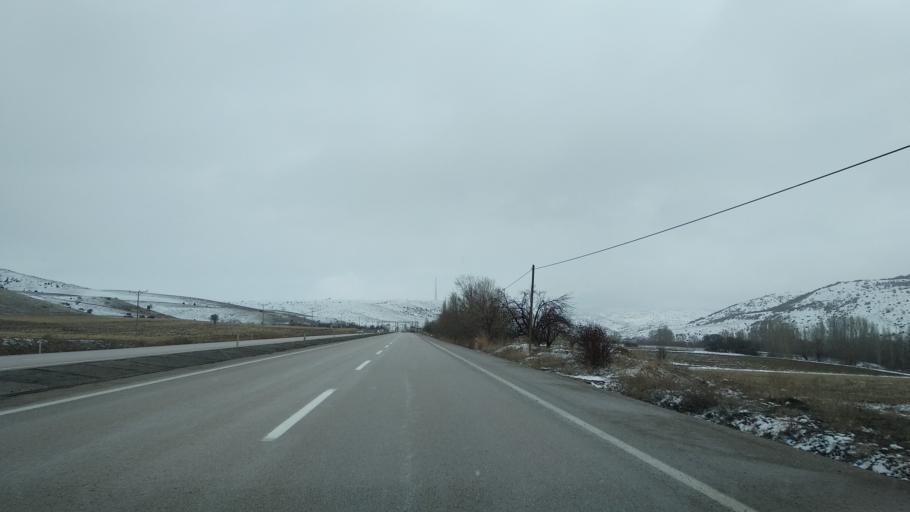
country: TR
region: Kayseri
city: Pinarbasi
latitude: 38.7172
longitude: 36.4237
